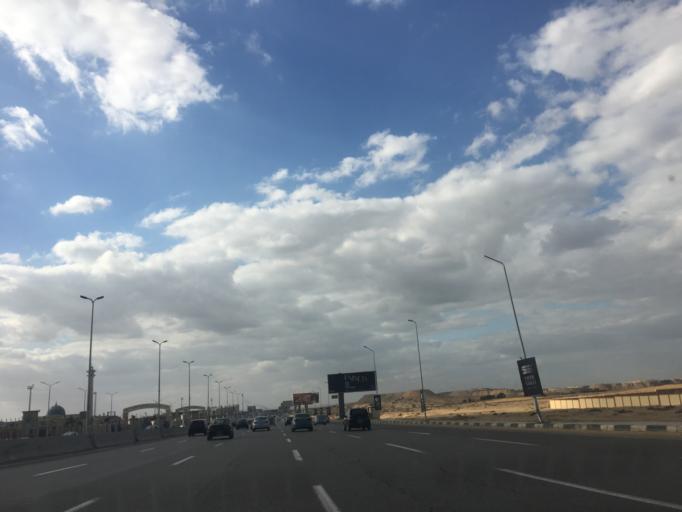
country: EG
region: Muhafazat al Qahirah
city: Cairo
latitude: 30.0178
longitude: 31.3890
